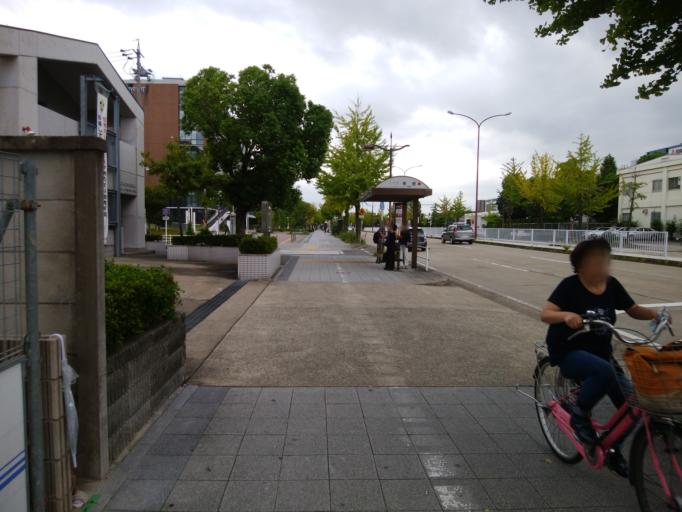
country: JP
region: Aichi
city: Nagoya-shi
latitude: 35.1902
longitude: 136.9436
